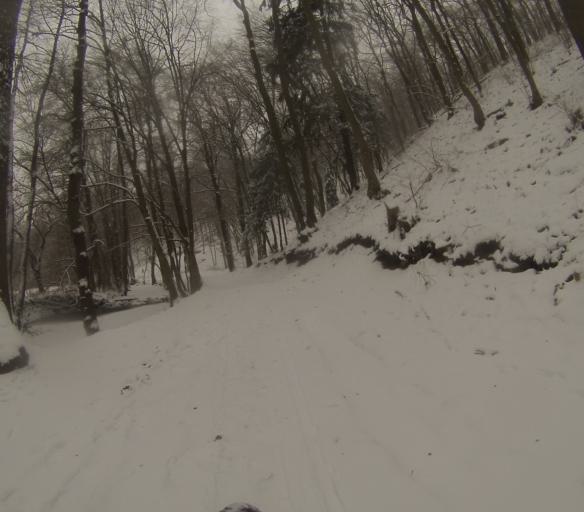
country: CZ
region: South Moravian
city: Strelice
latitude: 49.1313
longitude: 16.5077
